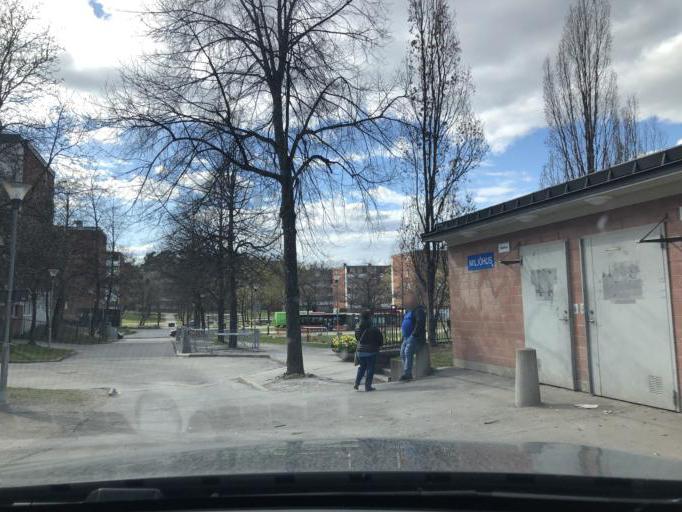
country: SE
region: Stockholm
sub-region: Botkyrka Kommun
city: Fittja
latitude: 59.2659
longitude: 17.8891
